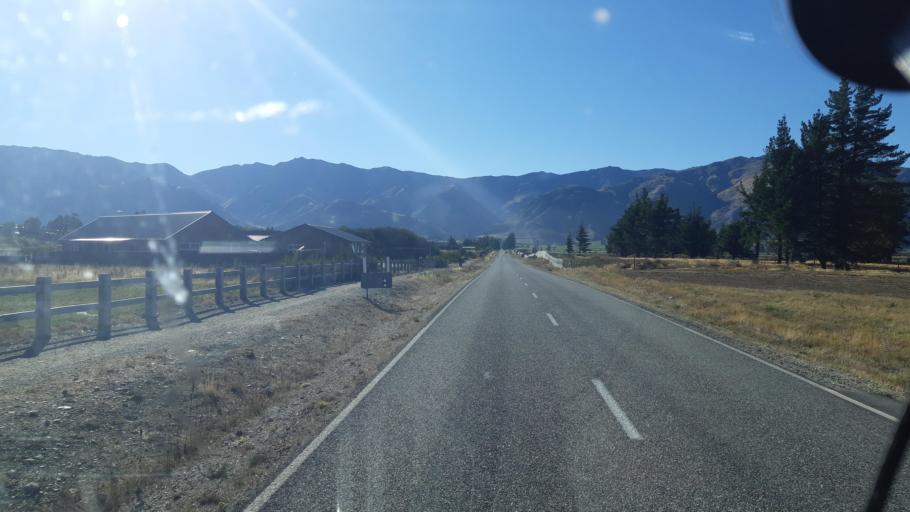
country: NZ
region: Otago
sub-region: Queenstown-Lakes District
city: Wanaka
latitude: -44.6184
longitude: 169.2582
